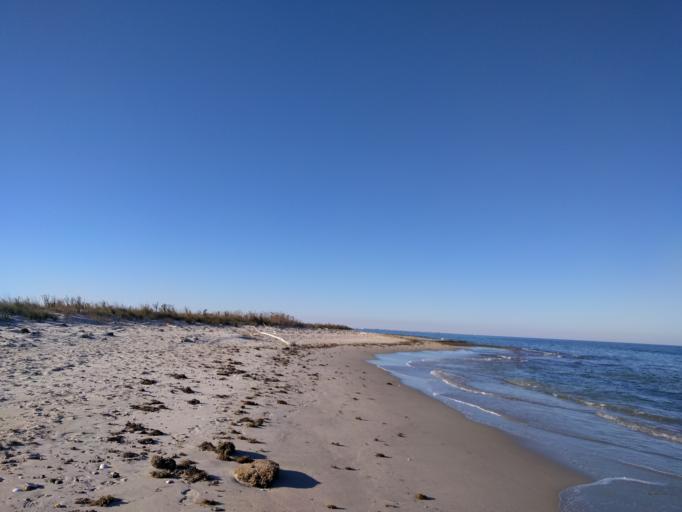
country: US
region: Virginia
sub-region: City of Poquoson
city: Poquoson
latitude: 37.0989
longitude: -76.2781
